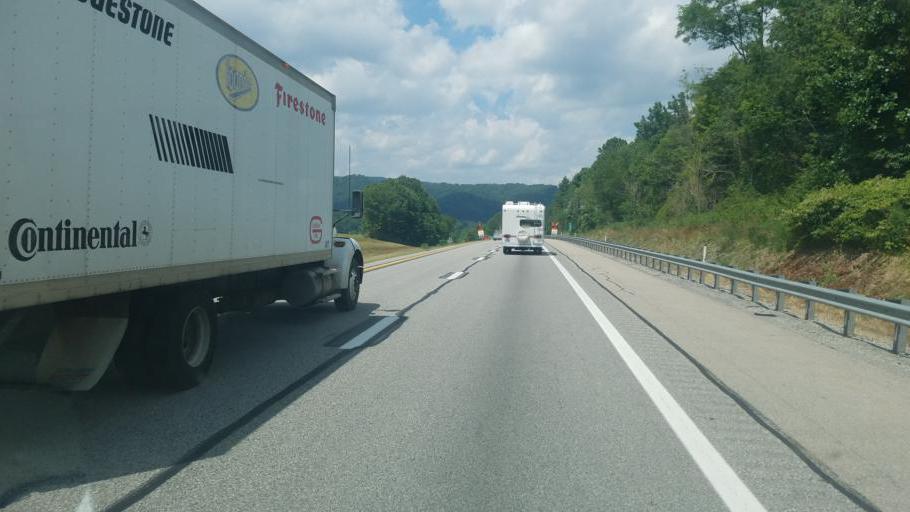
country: US
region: West Virginia
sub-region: Raleigh County
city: Bradley
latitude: 37.9081
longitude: -81.2664
